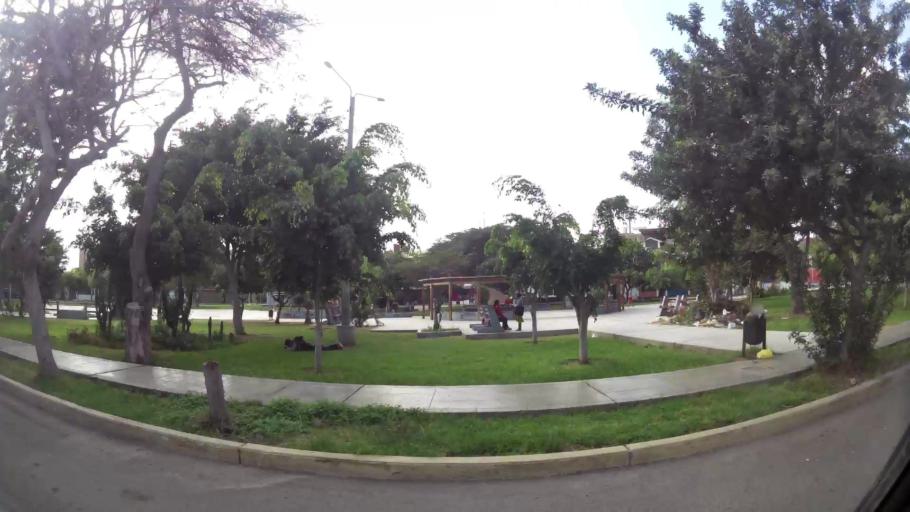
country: PE
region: La Libertad
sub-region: Provincia de Trujillo
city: Trujillo
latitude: -8.1066
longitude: -79.0119
